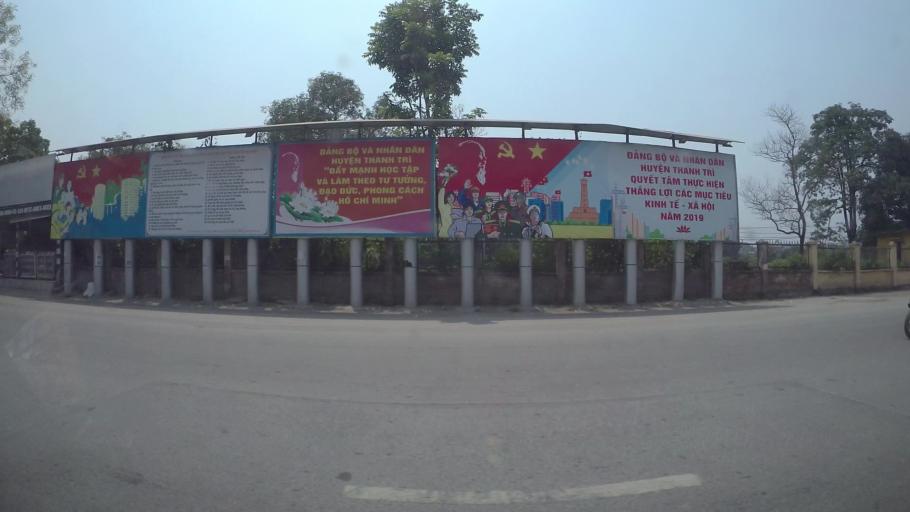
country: VN
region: Ha Noi
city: Van Dien
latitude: 20.9461
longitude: 105.8444
